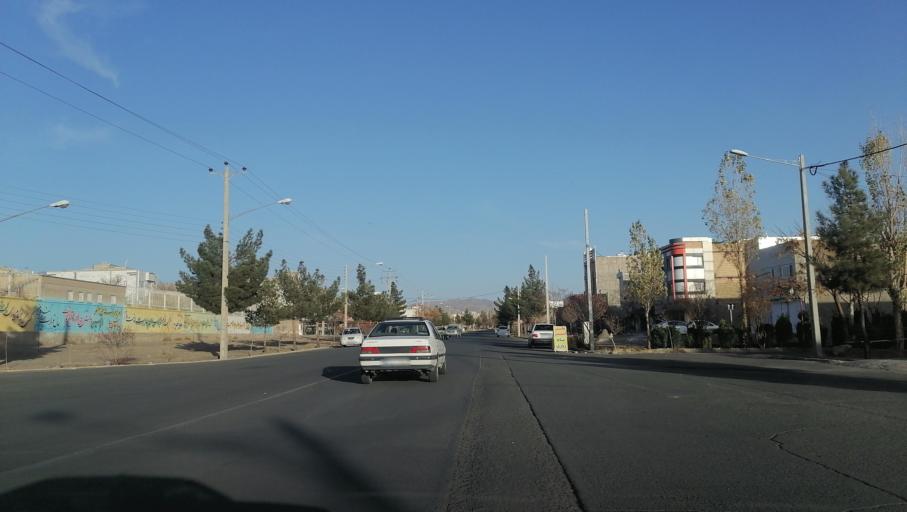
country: IR
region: Razavi Khorasan
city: Sabzevar
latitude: 36.2852
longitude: 57.6758
